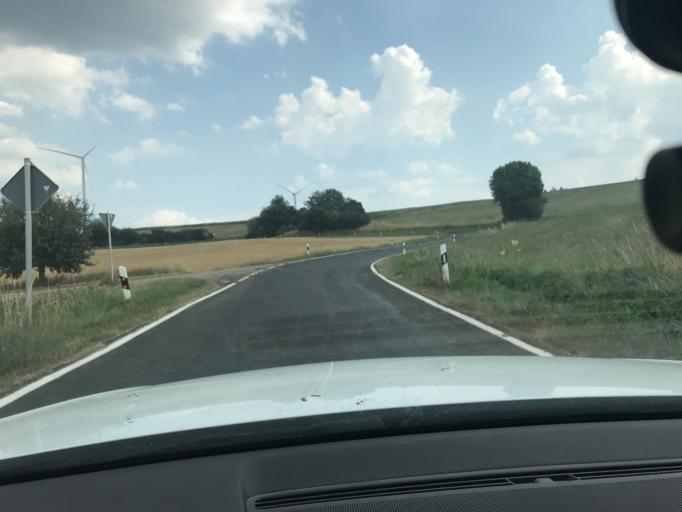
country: DE
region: Bavaria
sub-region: Upper Palatinate
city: Auerbach
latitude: 49.7394
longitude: 11.6375
